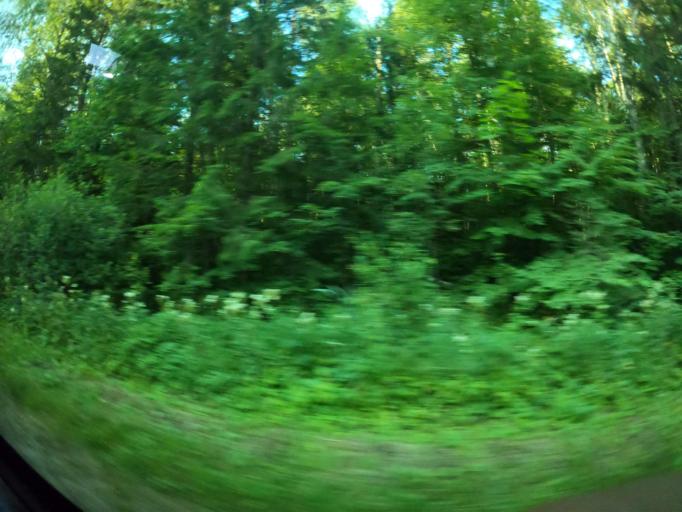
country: RU
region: Moskovskaya
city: Obolensk
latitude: 54.9869
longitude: 37.2098
